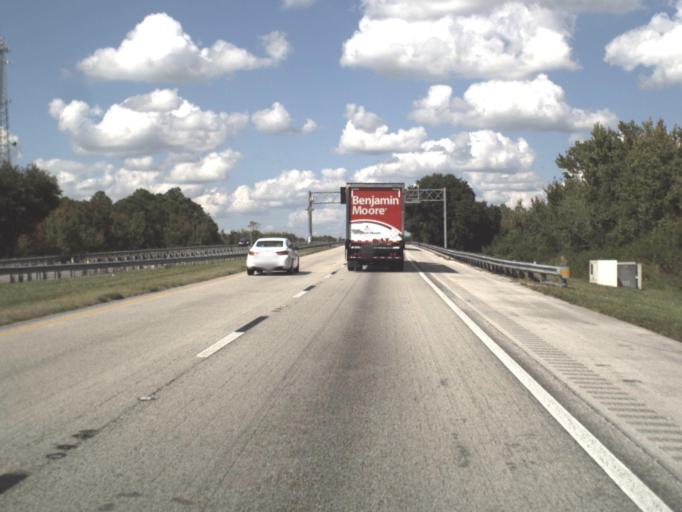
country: US
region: Florida
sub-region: Indian River County
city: Fellsmere
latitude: 27.5889
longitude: -80.8132
